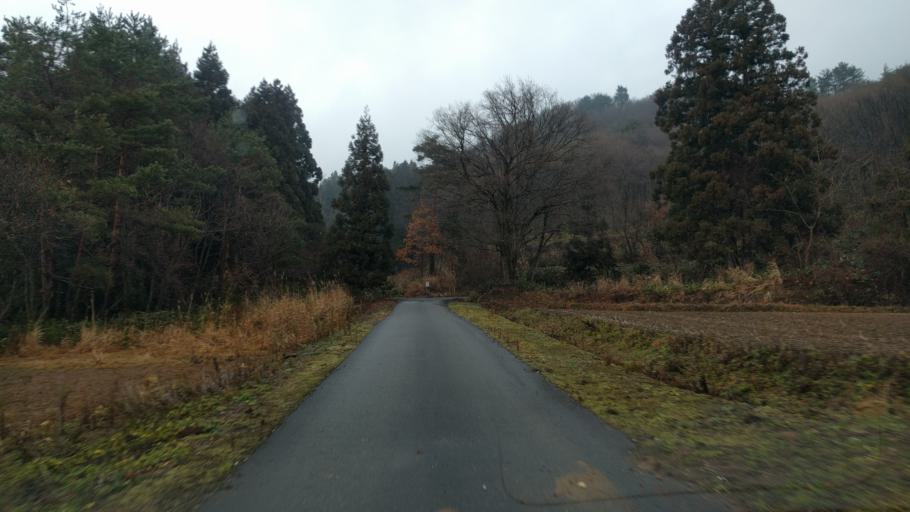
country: JP
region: Fukushima
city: Kitakata
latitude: 37.5809
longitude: 139.9677
